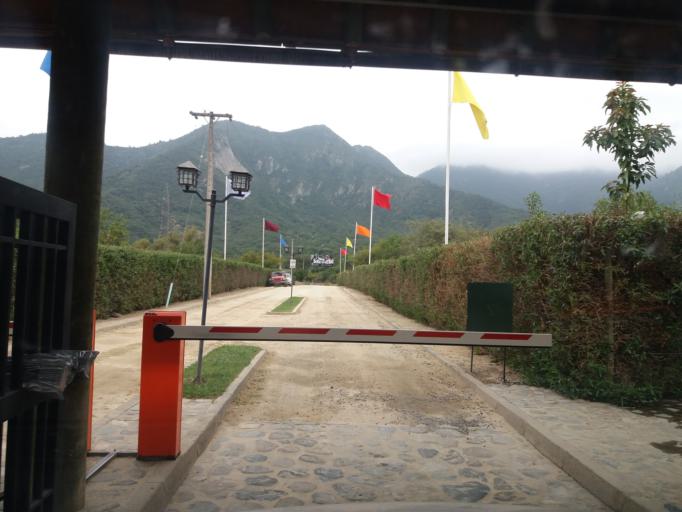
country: CL
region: Valparaiso
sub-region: Provincia de Marga Marga
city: Limache
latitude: -33.0290
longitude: -71.1428
